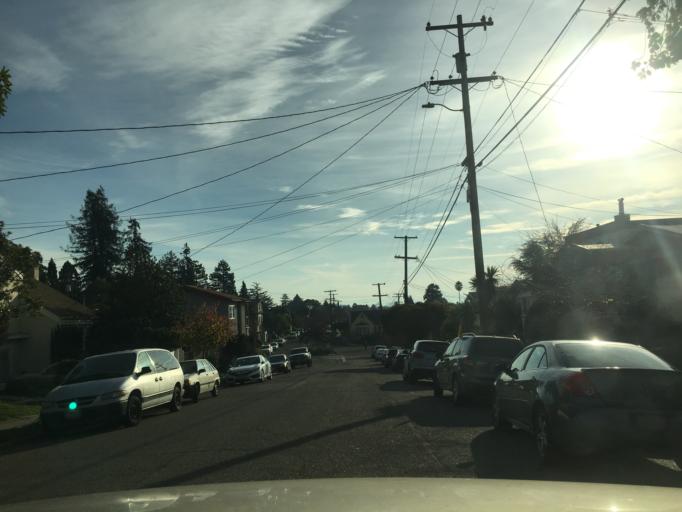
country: US
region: California
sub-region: Alameda County
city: Albany
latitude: 37.8846
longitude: -122.2854
